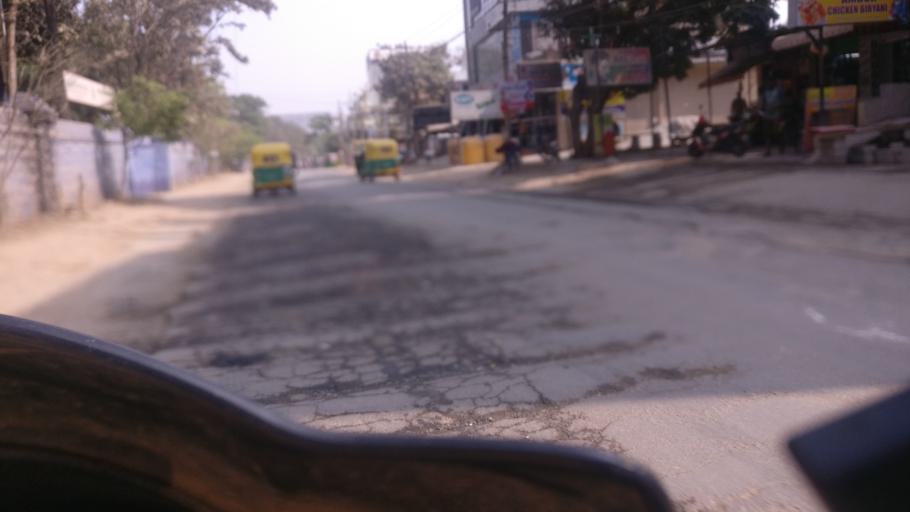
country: IN
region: Karnataka
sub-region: Bangalore Urban
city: Bangalore
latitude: 12.8850
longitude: 77.6723
